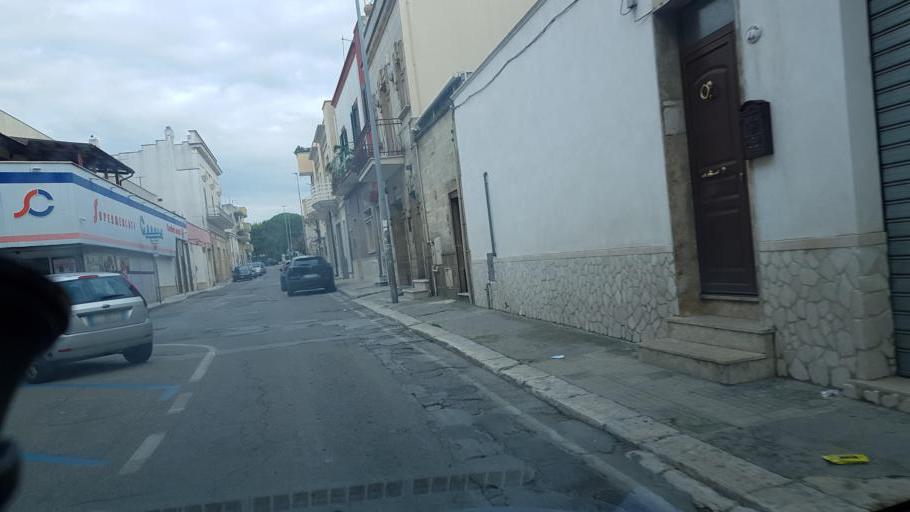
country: IT
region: Apulia
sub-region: Provincia di Brindisi
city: Oria
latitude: 40.4957
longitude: 17.6470
